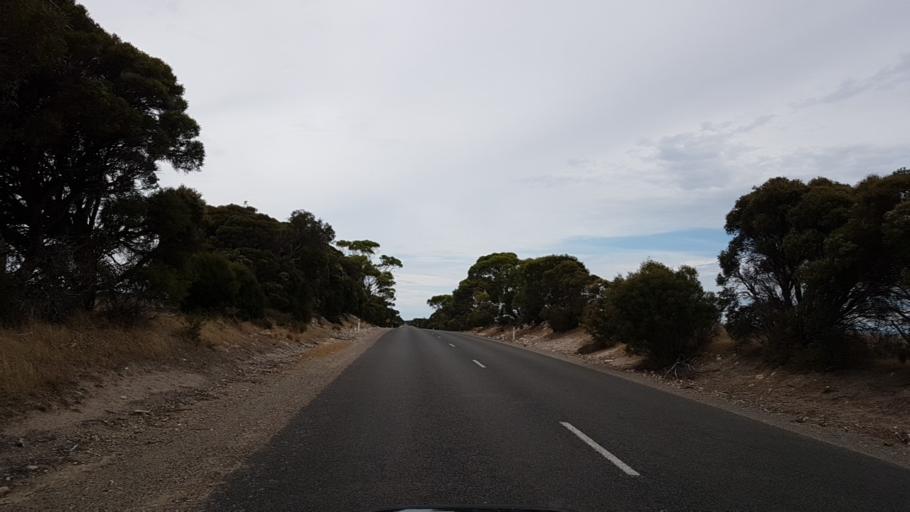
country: AU
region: South Australia
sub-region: Yorke Peninsula
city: Honiton
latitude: -34.9491
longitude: 137.0981
